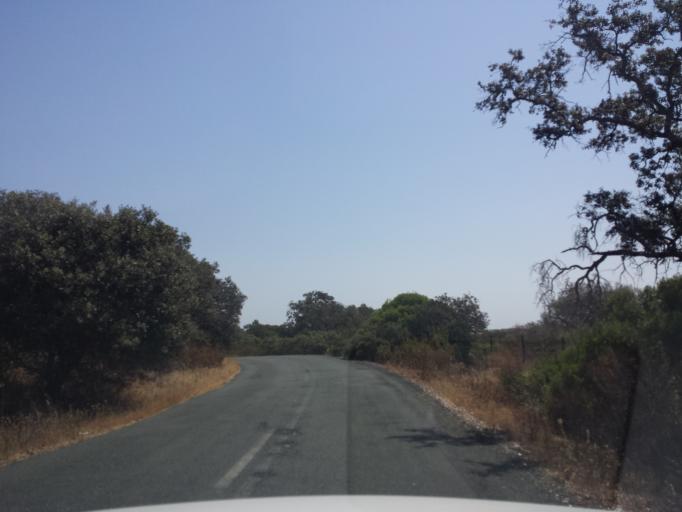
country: ES
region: Andalusia
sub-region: Provincia de Sevilla
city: Castilblanco de los Arroyos
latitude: 37.6960
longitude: -5.9476
